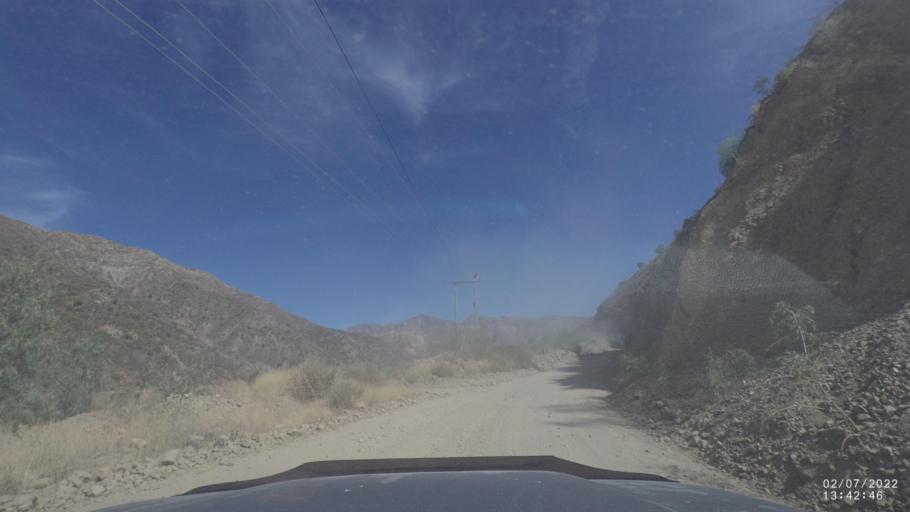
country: BO
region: Cochabamba
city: Irpa Irpa
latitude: -17.8018
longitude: -66.3564
